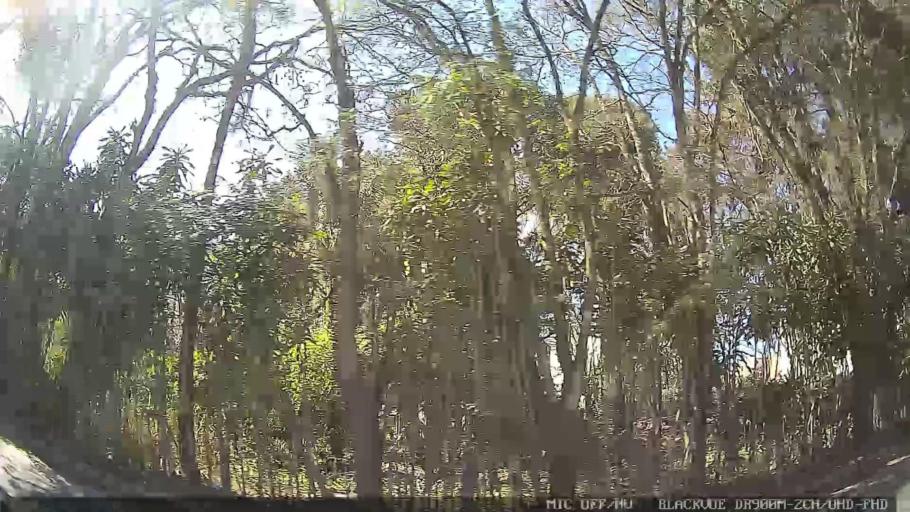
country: BR
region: Sao Paulo
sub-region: Jacarei
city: Jacarei
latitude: -23.3356
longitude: -46.0014
